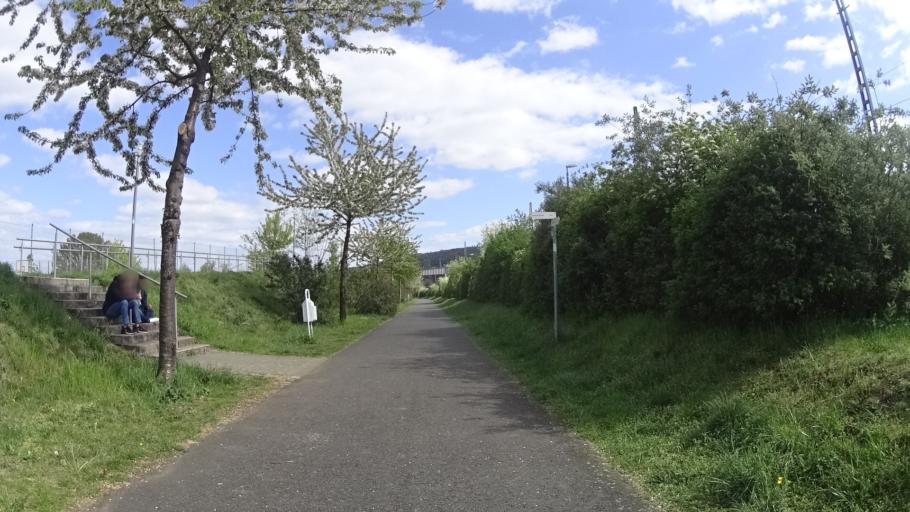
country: DE
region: Rheinland-Pfalz
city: Bingen am Rhein
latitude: 49.9695
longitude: 7.8828
